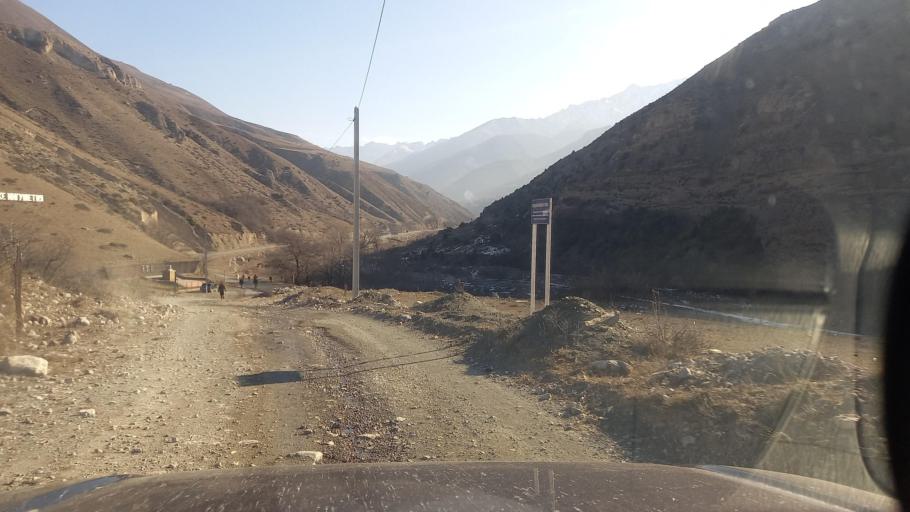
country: RU
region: Ingushetiya
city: Dzhayrakh
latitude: 42.8433
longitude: 44.6519
